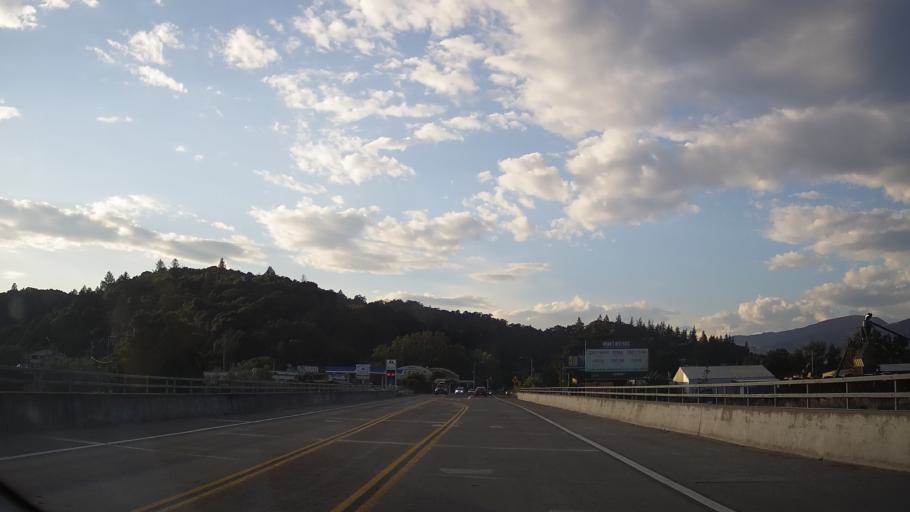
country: US
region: California
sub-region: Mendocino County
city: Talmage
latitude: 38.9683
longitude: -123.1159
